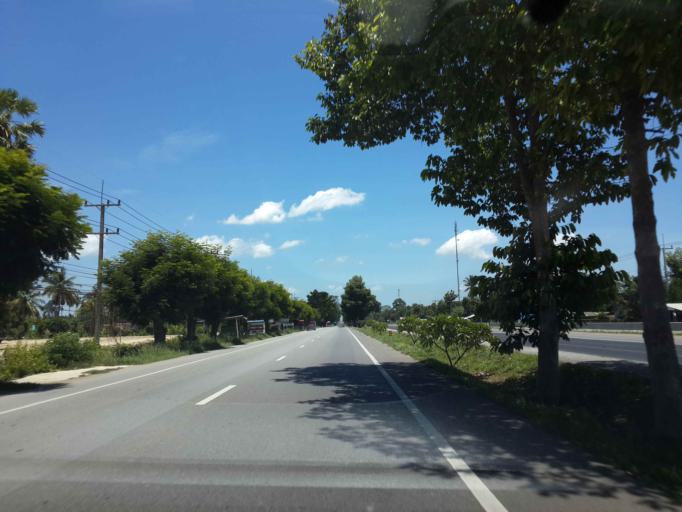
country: TH
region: Phetchaburi
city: Tha Yang
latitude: 13.0017
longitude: 99.9102
